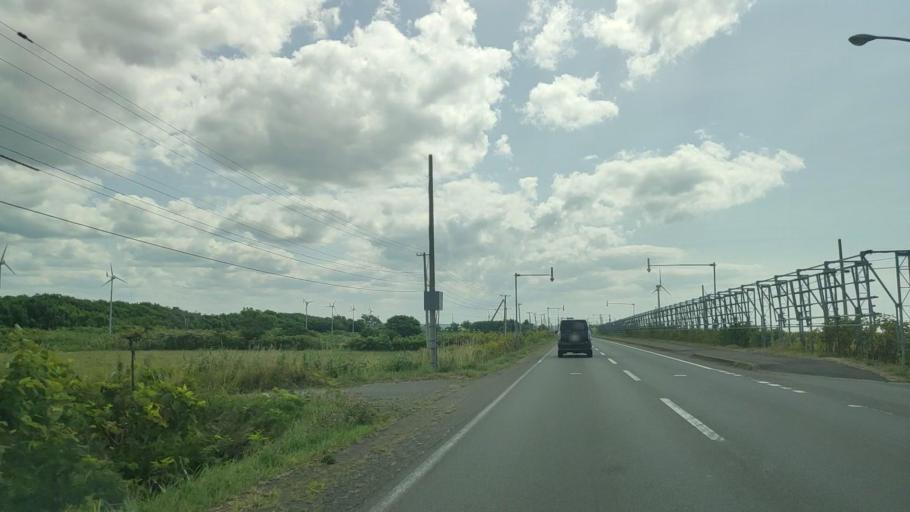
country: JP
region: Hokkaido
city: Makubetsu
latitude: 44.7589
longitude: 141.7943
